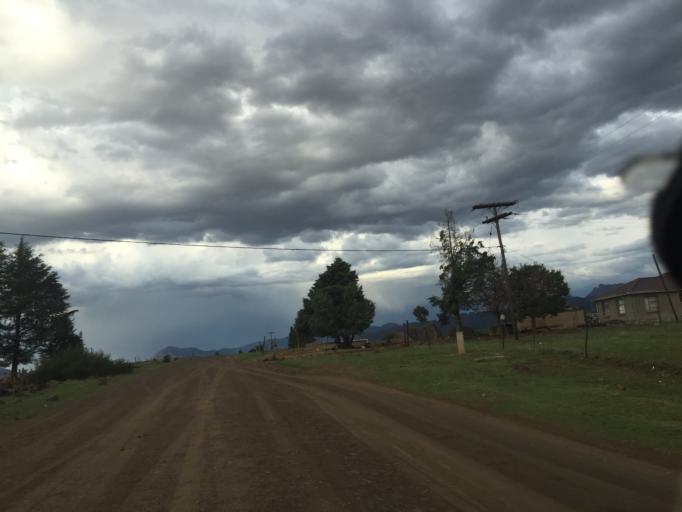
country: LS
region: Leribe
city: Leribe
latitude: -29.1529
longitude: 28.0396
